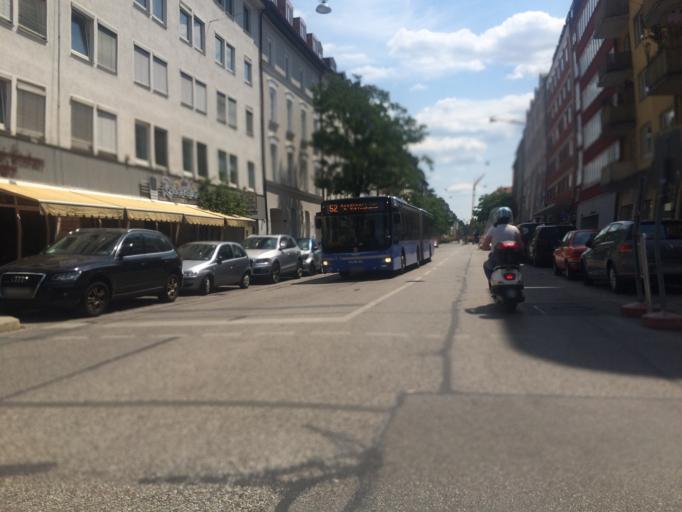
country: DE
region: Bavaria
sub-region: Upper Bavaria
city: Munich
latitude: 48.1330
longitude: 11.5743
